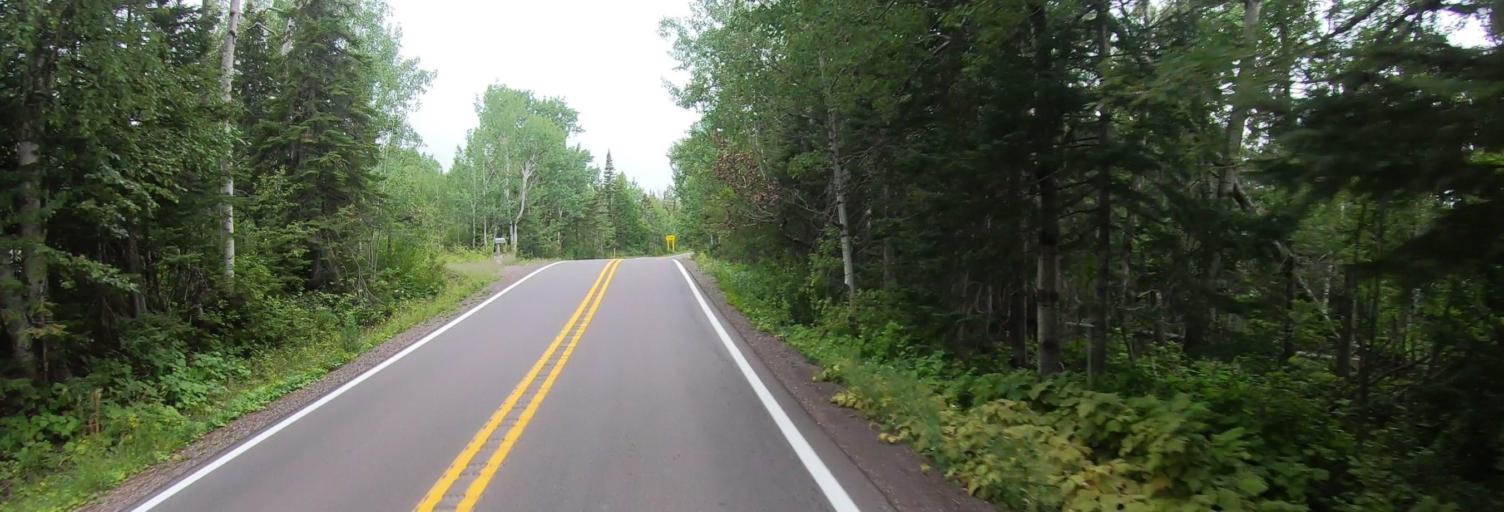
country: US
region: Michigan
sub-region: Keweenaw County
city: Eagle River
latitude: 47.4787
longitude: -87.9545
